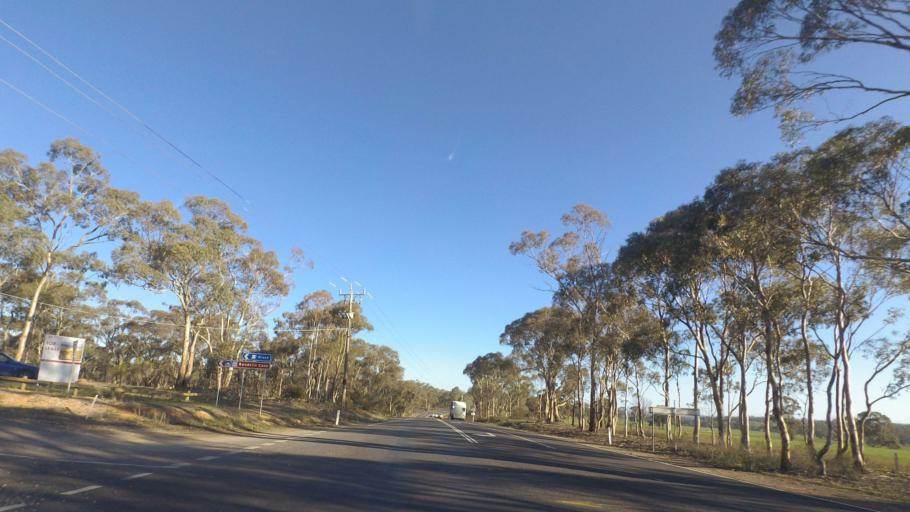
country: AU
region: Victoria
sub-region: Greater Bendigo
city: Kennington
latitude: -36.8563
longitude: 144.5062
